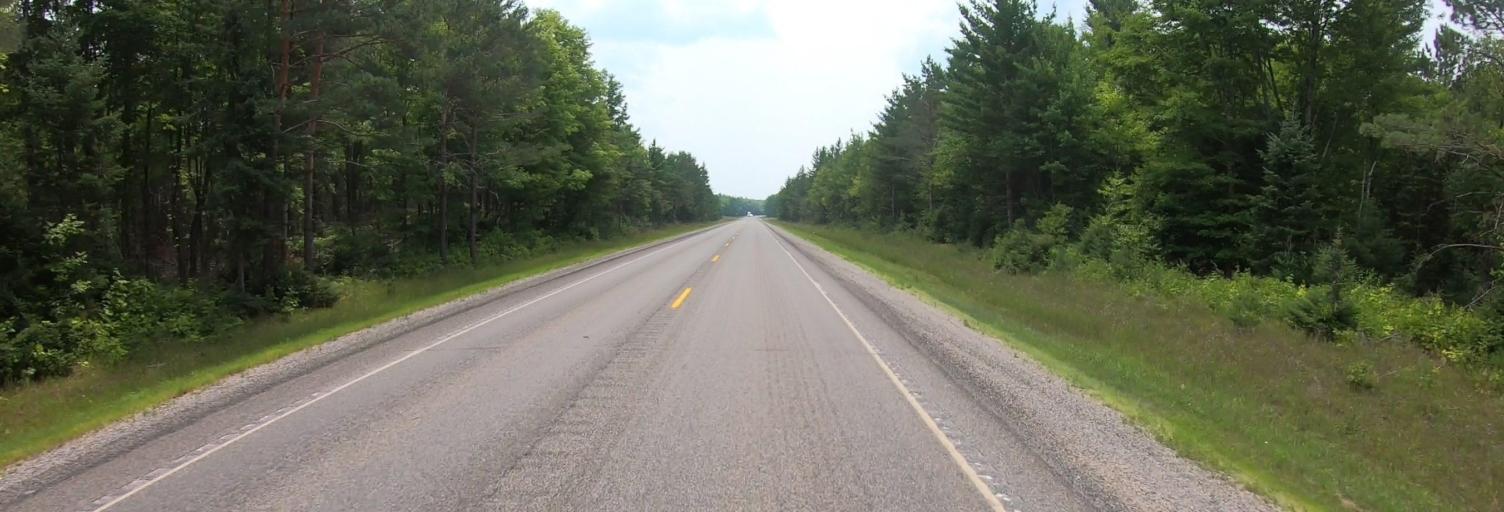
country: US
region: Michigan
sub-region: Alger County
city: Munising
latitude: 46.3441
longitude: -86.7298
